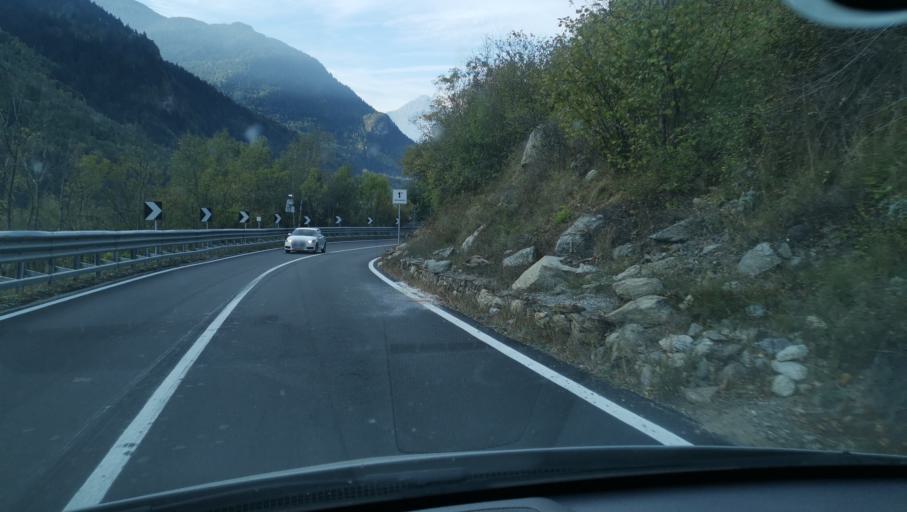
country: IT
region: Piedmont
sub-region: Provincia di Torino
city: Salbertrand
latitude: 45.0801
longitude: 6.9023
